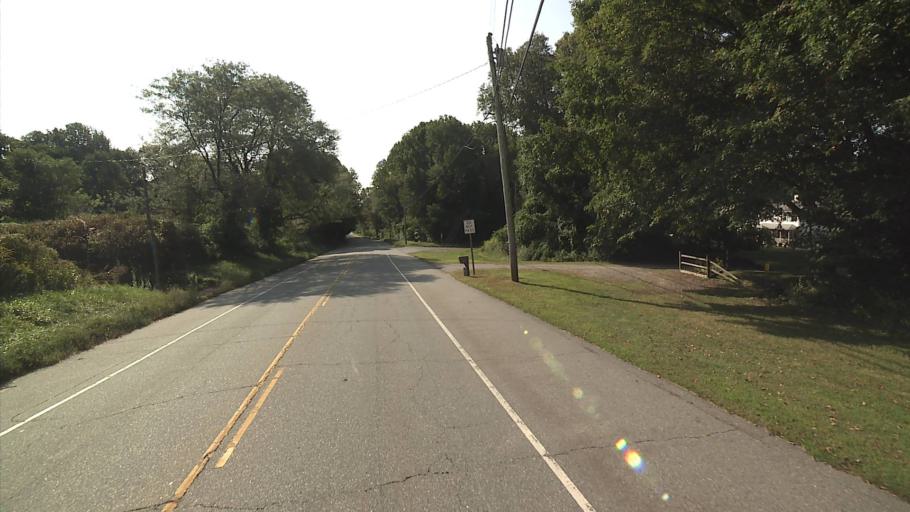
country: US
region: Connecticut
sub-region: New London County
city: Baltic
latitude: 41.5946
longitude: -72.1627
